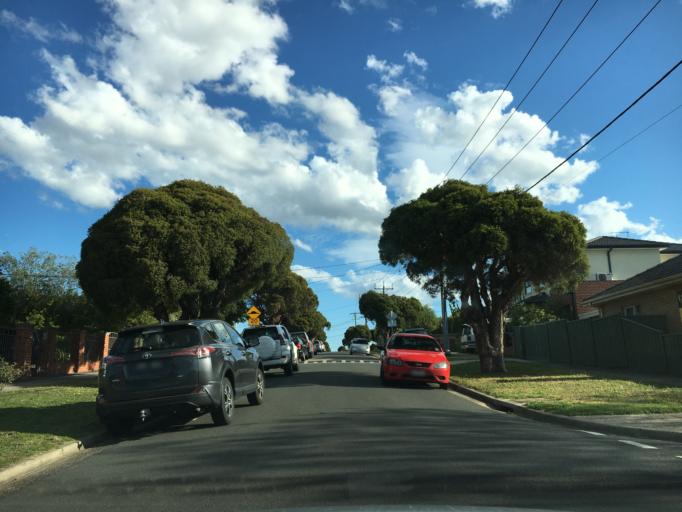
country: AU
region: Victoria
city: Clayton
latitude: -37.9006
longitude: 145.1130
